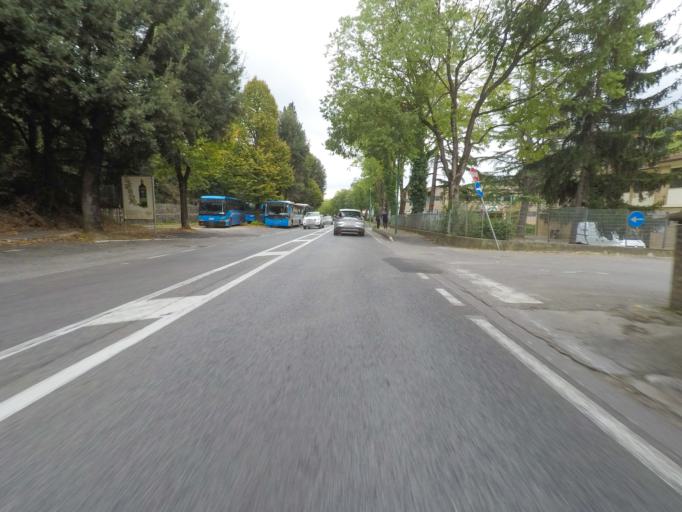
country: IT
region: Tuscany
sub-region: Provincia di Siena
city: Siena
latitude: 43.3248
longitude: 11.3438
